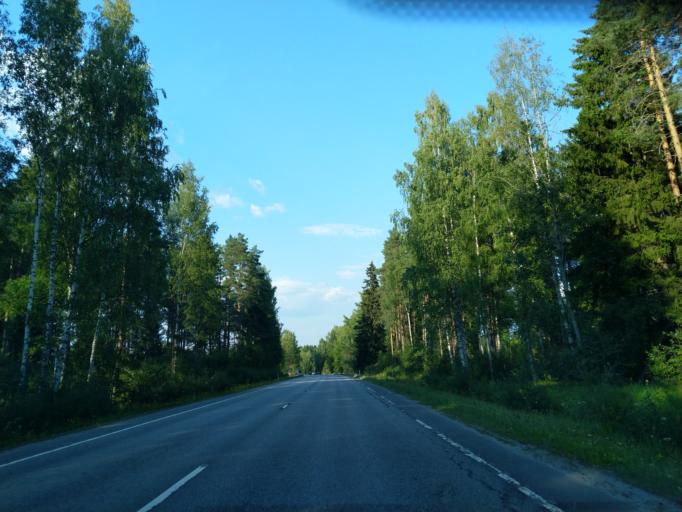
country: FI
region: Satakunta
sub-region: Pori
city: Laengelmaeki
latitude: 61.7545
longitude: 22.1272
